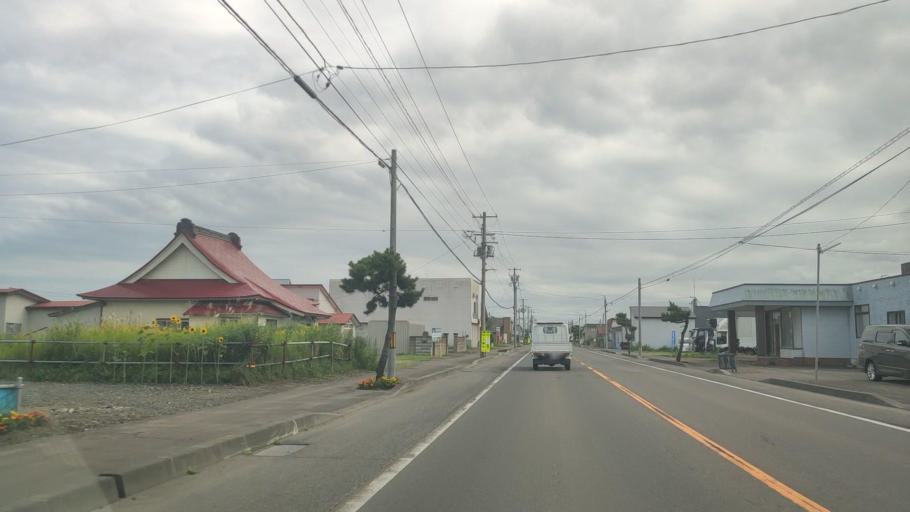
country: JP
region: Hokkaido
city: Niseko Town
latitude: 42.4378
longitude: 140.3230
